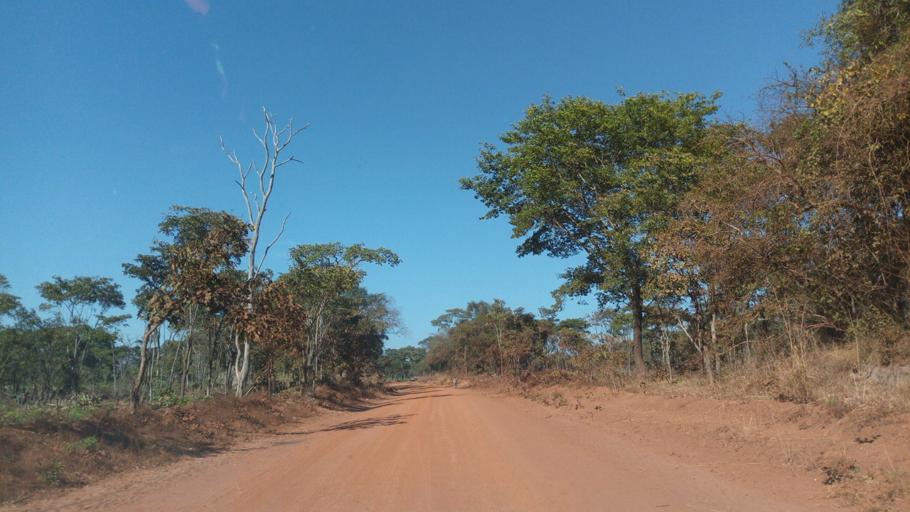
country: ZM
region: Luapula
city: Mwense
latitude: -10.6734
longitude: 28.4073
